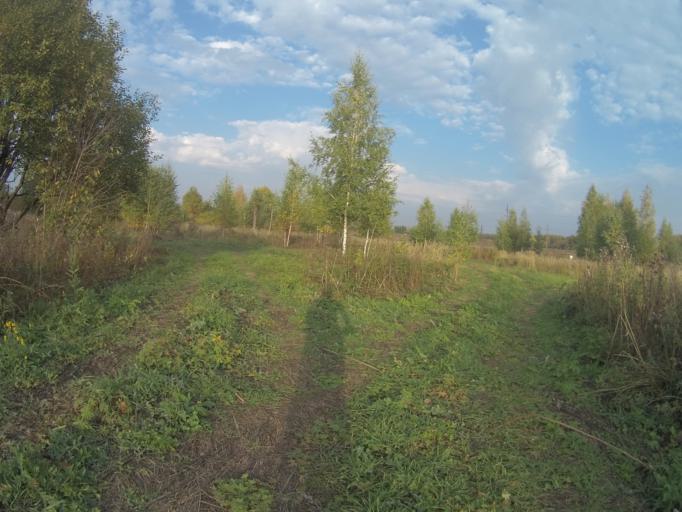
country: RU
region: Vladimir
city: Bogolyubovo
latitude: 56.1770
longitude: 40.4878
